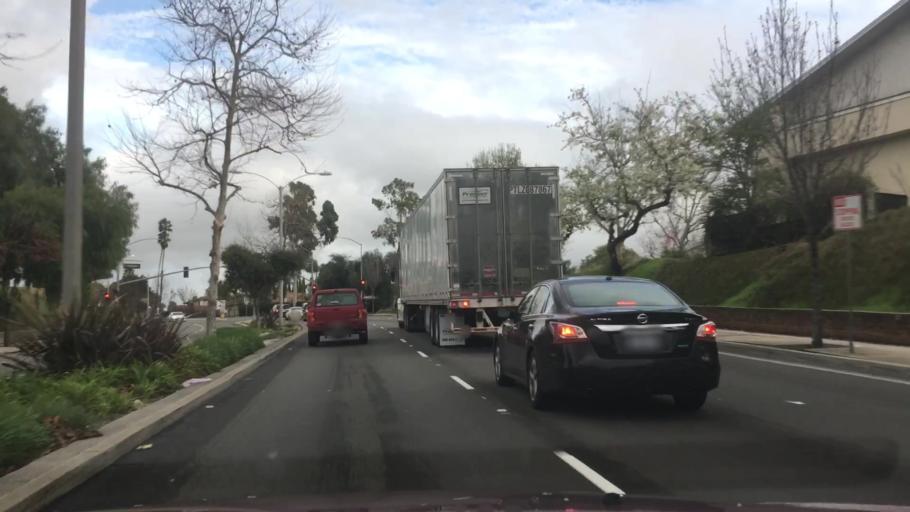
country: US
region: California
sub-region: Los Angeles County
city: La Mirada
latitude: 33.9164
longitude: -118.0071
